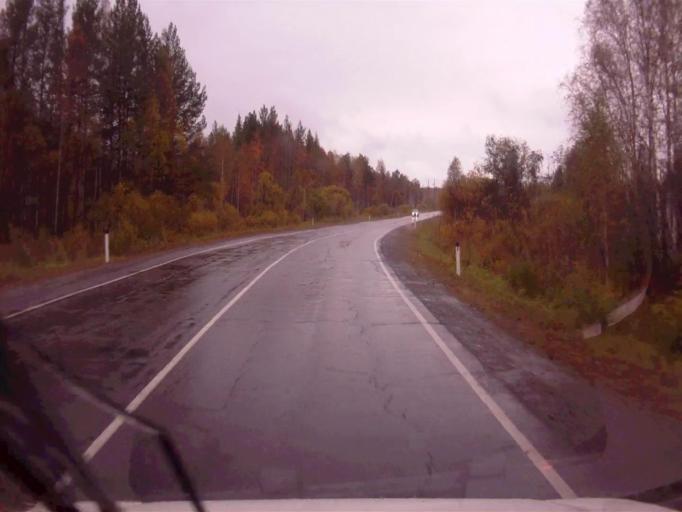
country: RU
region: Chelyabinsk
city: Verkhniy Ufaley
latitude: 55.9893
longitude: 60.3350
